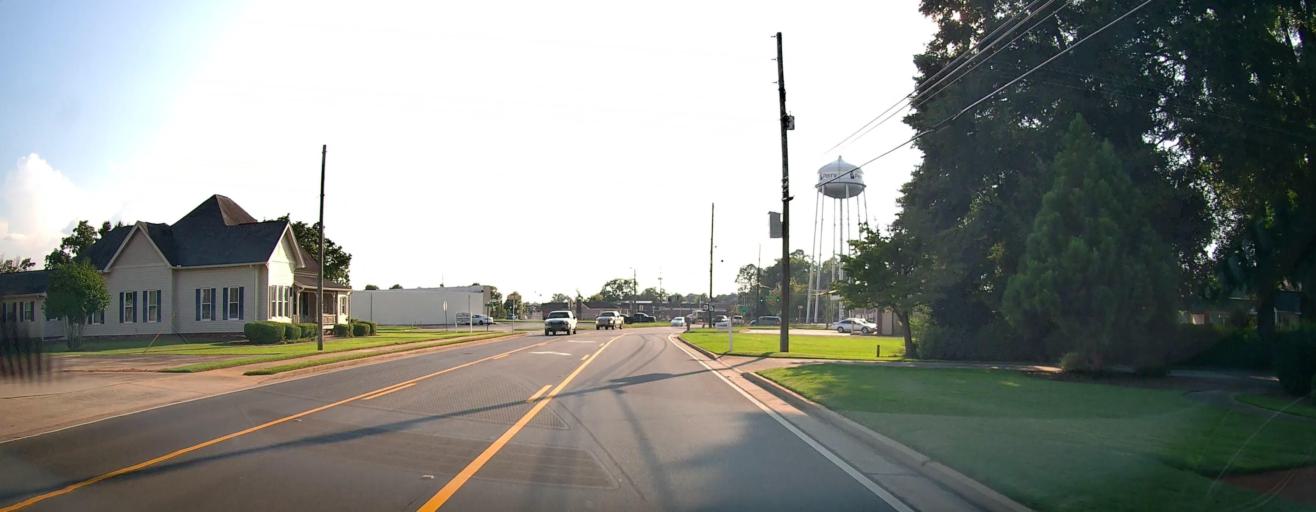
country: US
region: Georgia
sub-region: Houston County
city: Perry
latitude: 32.4609
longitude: -83.7293
